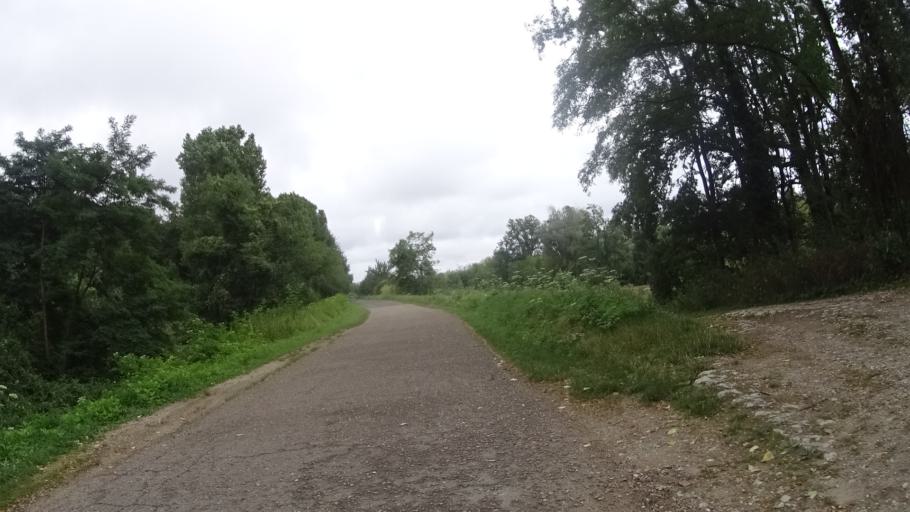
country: FR
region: Centre
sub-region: Departement du Loir-et-Cher
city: La Chaussee-Saint-Victor
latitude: 47.6165
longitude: 1.3788
